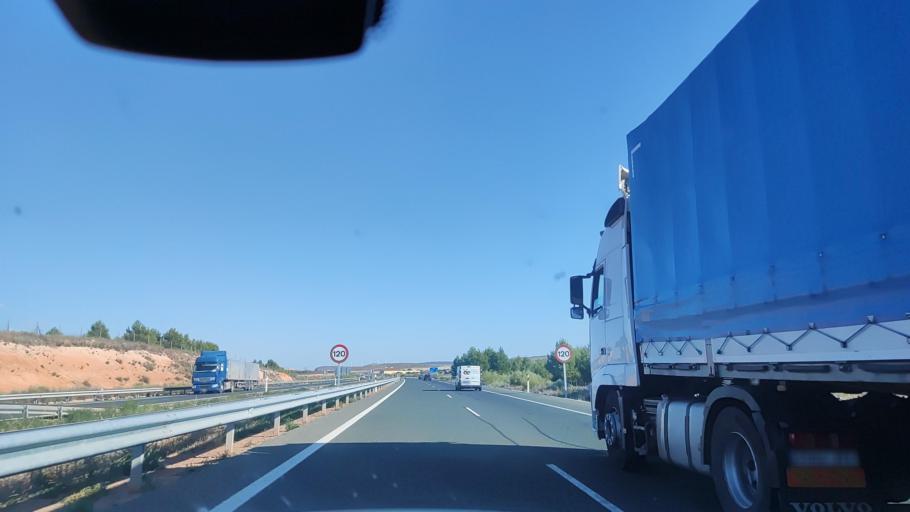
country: ES
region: Castille-La Mancha
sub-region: Provincia de Albacete
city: Pozo-Canada
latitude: 38.8466
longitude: -1.7642
